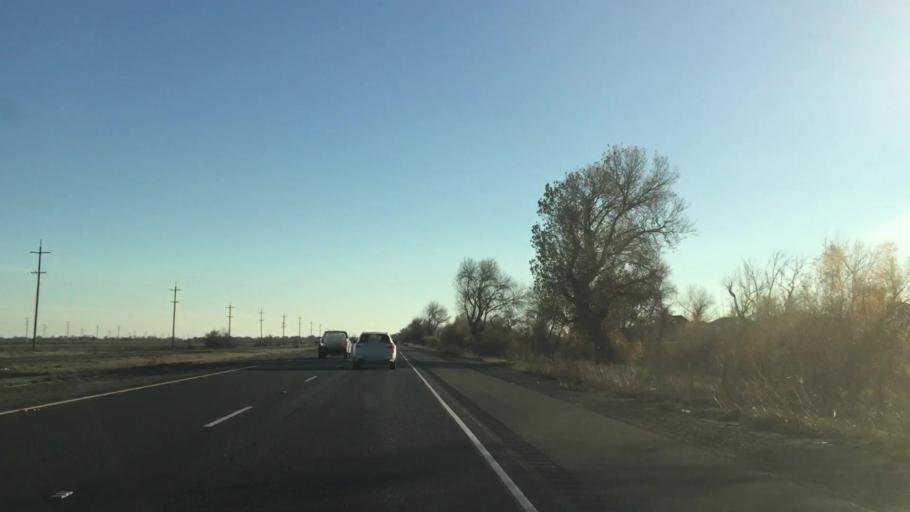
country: US
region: California
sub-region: Yuba County
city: Plumas Lake
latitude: 39.0032
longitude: -121.5435
